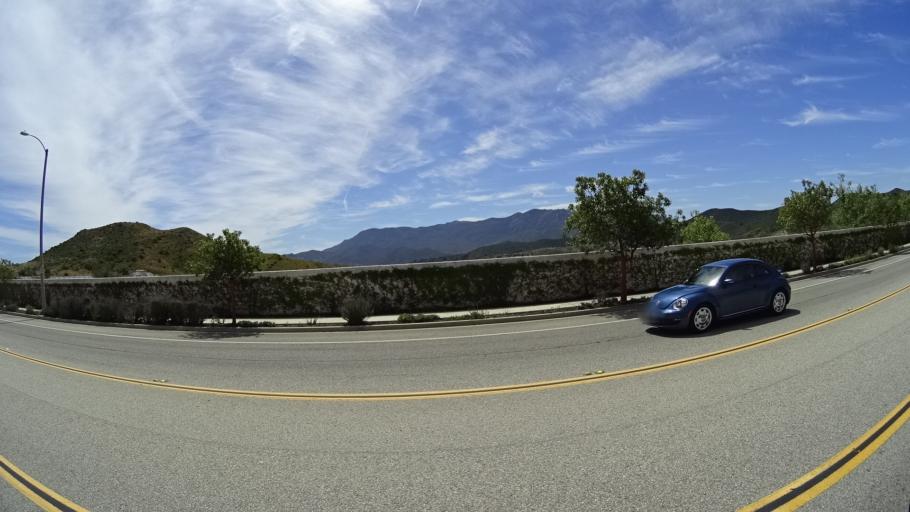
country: US
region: California
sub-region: Ventura County
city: Casa Conejo
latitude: 34.1797
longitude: -118.9746
